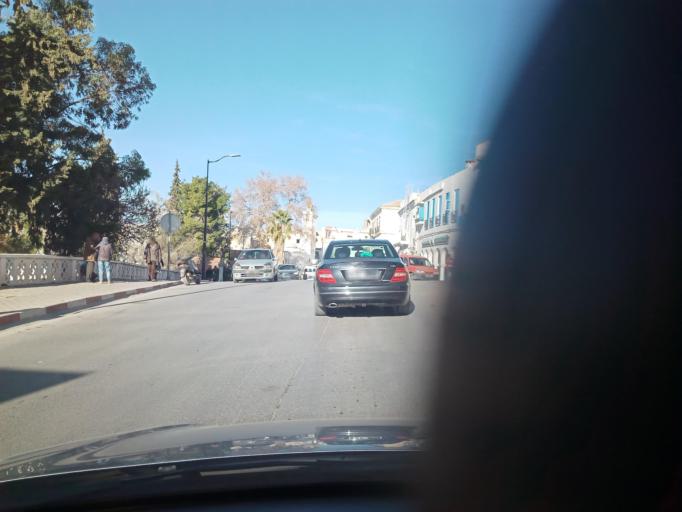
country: TN
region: Kef
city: El Kef
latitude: 36.1798
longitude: 8.7118
